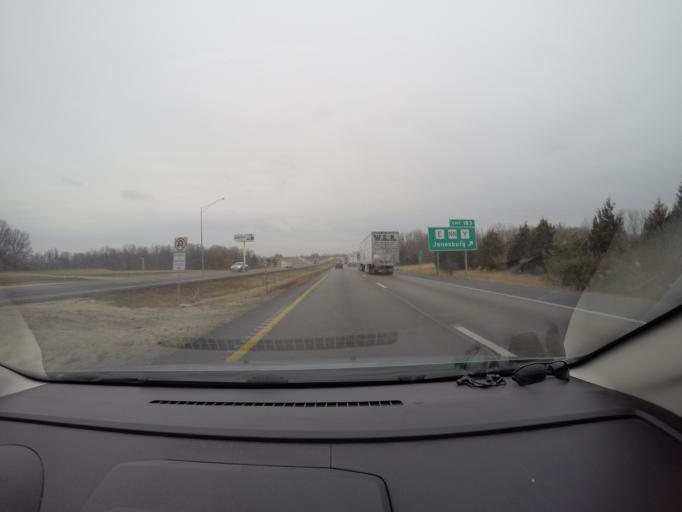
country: US
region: Missouri
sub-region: Warren County
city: Warrenton
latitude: 38.8598
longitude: -91.3099
